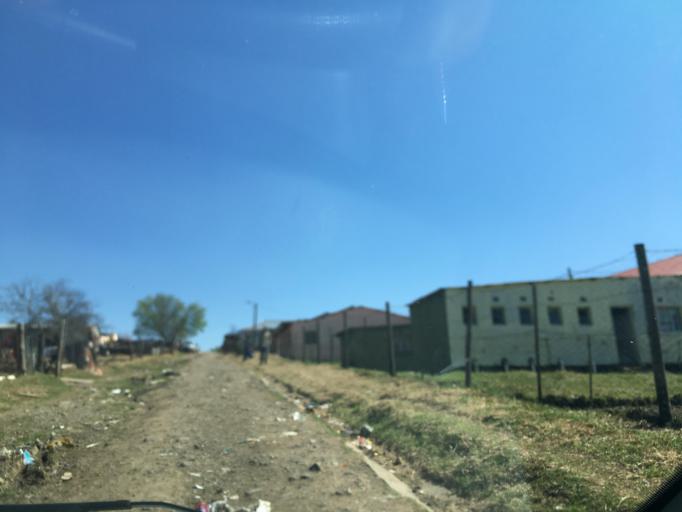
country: ZA
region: Eastern Cape
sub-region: Chris Hani District Municipality
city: Elliot
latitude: -31.3318
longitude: 27.8257
